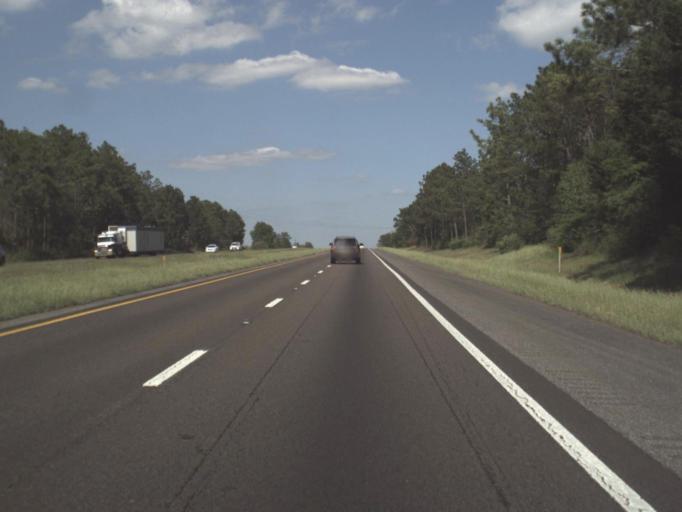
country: US
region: Florida
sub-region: Santa Rosa County
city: East Milton
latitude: 30.6650
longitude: -86.8593
